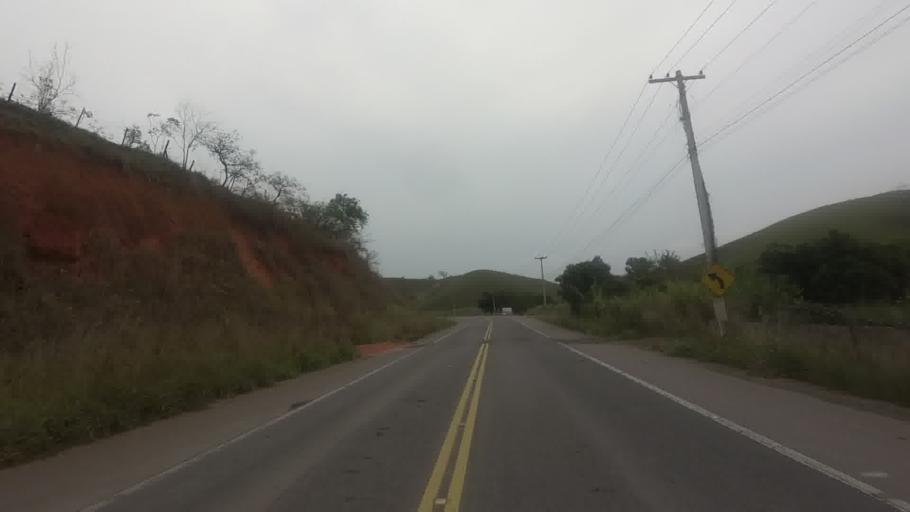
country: BR
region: Rio de Janeiro
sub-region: Santo Antonio De Padua
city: Santo Antonio de Padua
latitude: -21.6042
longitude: -42.2425
